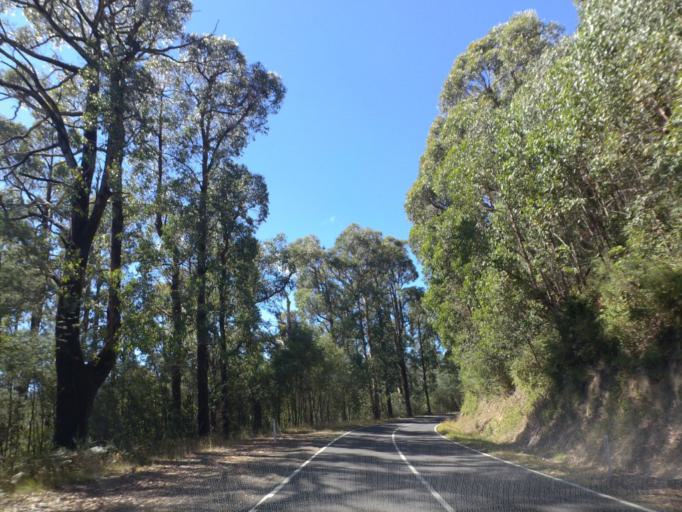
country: AU
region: Victoria
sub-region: Yarra Ranges
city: Millgrove
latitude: -37.5228
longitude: 145.8042
